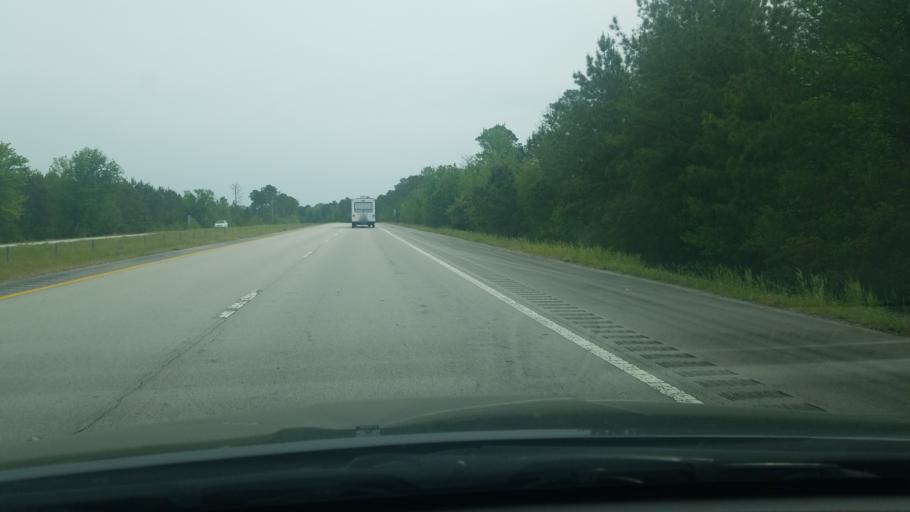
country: US
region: North Carolina
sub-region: Craven County
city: River Bend
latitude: 35.1051
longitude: -77.1655
